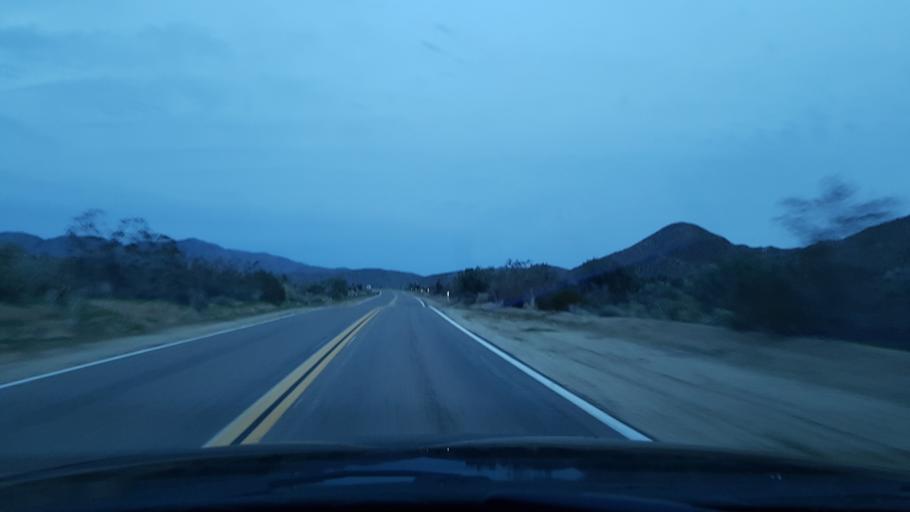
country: US
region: California
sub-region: San Diego County
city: Julian
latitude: 33.0178
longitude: -116.4313
